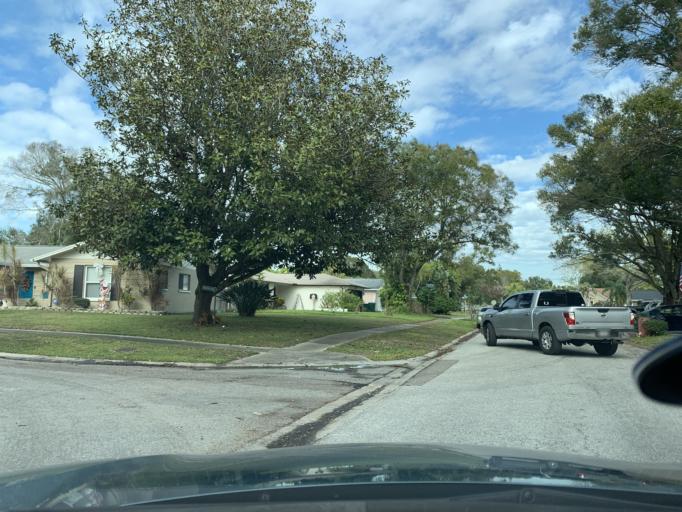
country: US
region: Florida
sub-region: Pinellas County
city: Kenneth City
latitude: 27.8259
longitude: -82.7353
